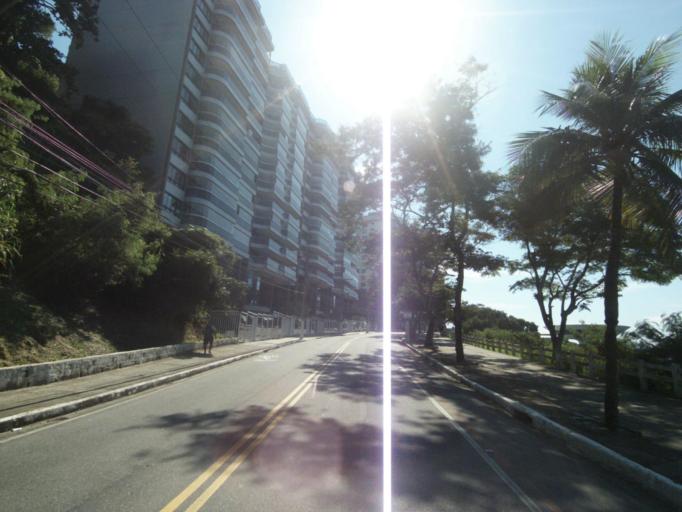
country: BR
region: Rio de Janeiro
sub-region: Niteroi
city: Niteroi
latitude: -22.9079
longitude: -43.1291
